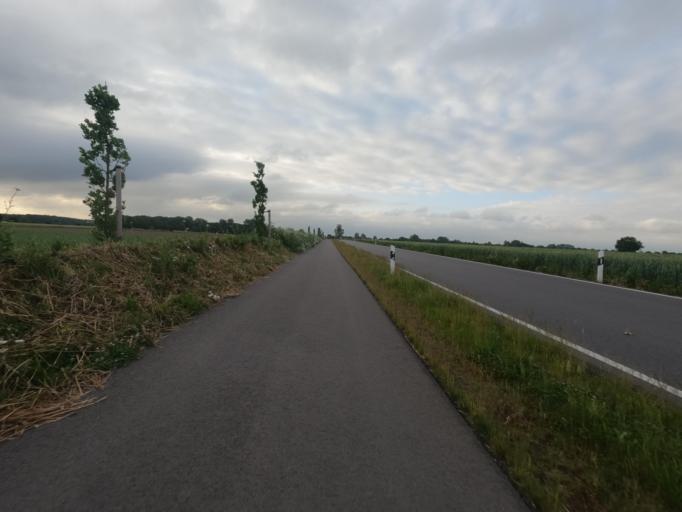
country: NL
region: Limburg
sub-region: Gemeente Roerdalen
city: Vlodrop
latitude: 51.1162
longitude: 6.1097
